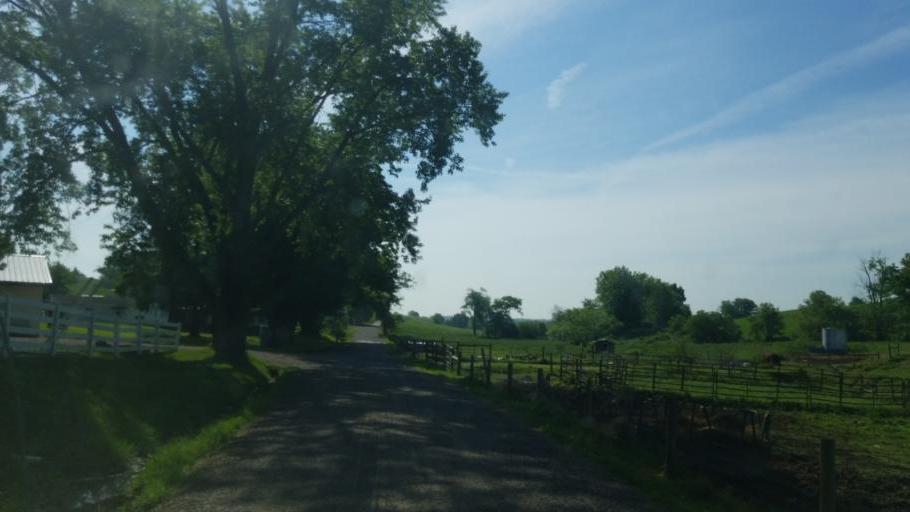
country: US
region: Ohio
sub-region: Tuscarawas County
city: Sugarcreek
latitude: 40.4813
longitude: -81.7626
